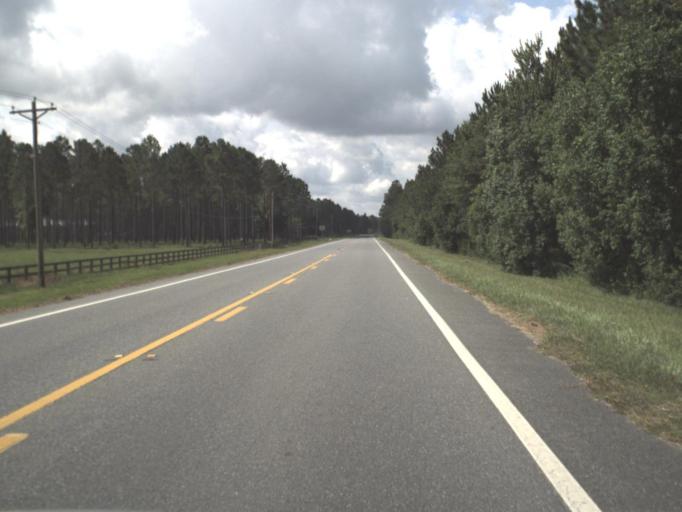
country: US
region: Florida
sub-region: Baker County
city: Macclenny
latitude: 30.3221
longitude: -82.1250
